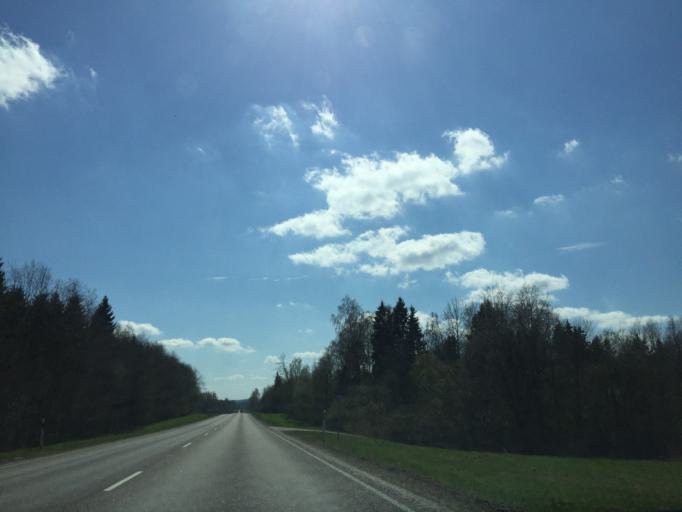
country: EE
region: Tartu
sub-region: Elva linn
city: Elva
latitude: 58.1065
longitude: 26.2368
